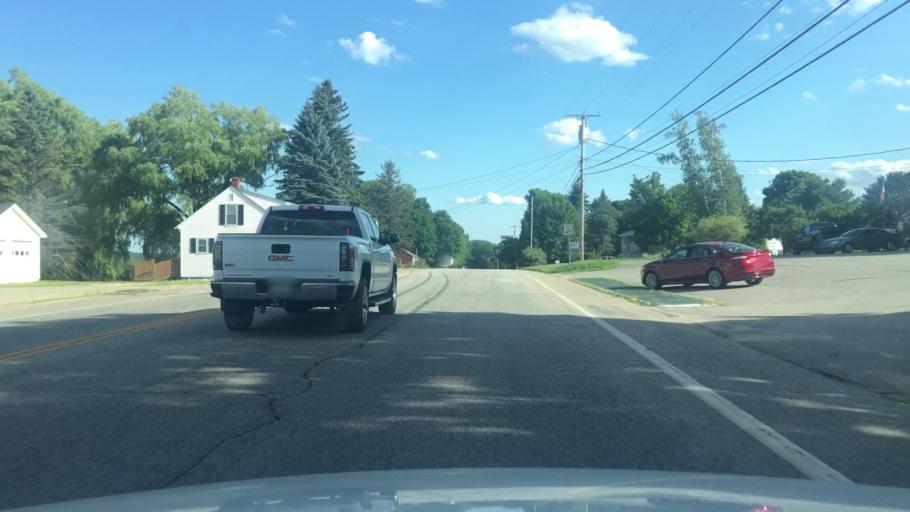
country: US
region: Maine
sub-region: Franklin County
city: Jay
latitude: 44.5174
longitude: -70.2238
